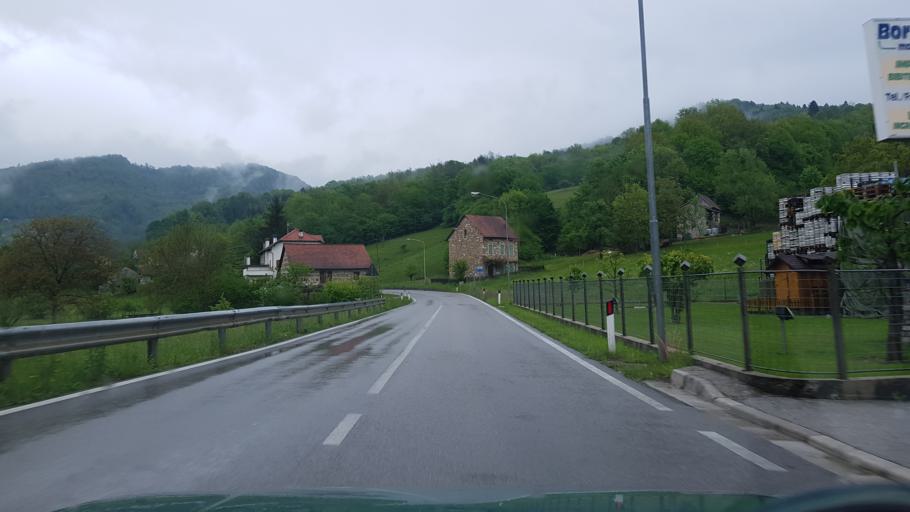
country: IT
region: Veneto
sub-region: Provincia di Belluno
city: Puos d'Alpago
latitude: 46.1380
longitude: 12.3722
